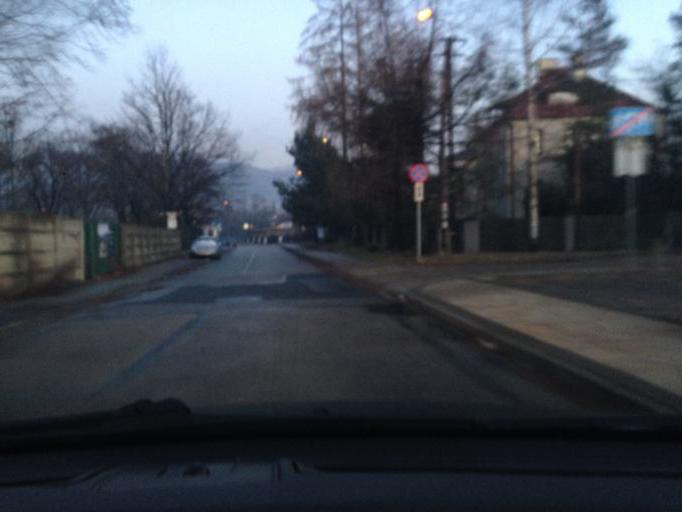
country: PL
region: Silesian Voivodeship
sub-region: Powiat bielski
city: Bystra
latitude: 49.7901
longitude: 19.0563
